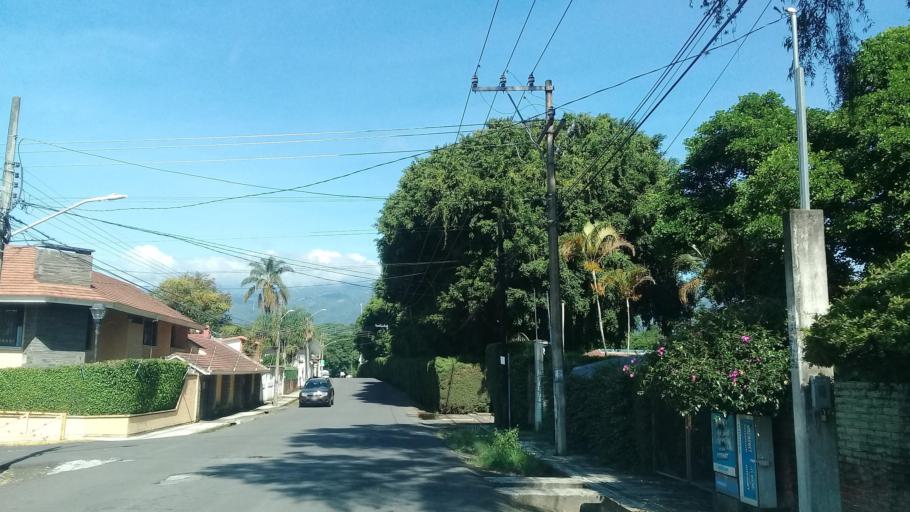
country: MX
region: Veracruz
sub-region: Xalapa
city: Xalapa de Enriquez
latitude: 19.5281
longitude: -96.9454
